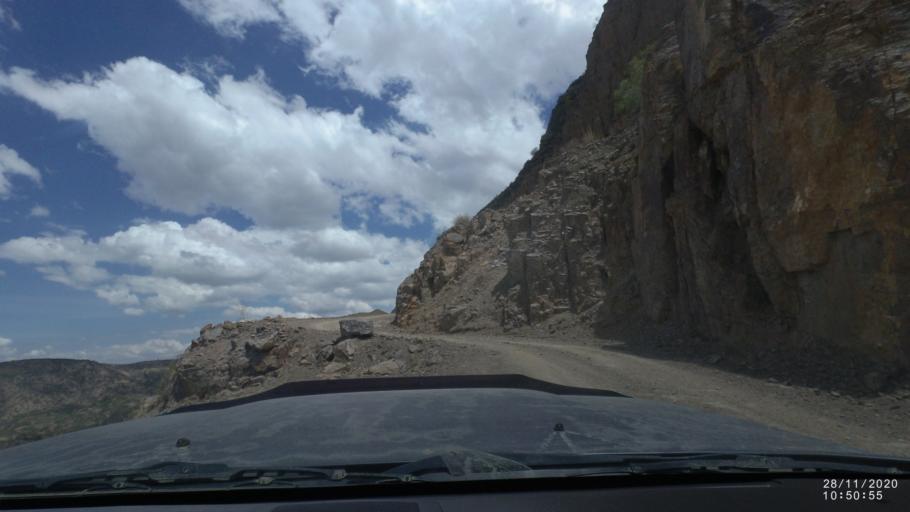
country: BO
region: Cochabamba
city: Capinota
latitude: -17.7847
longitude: -66.1235
